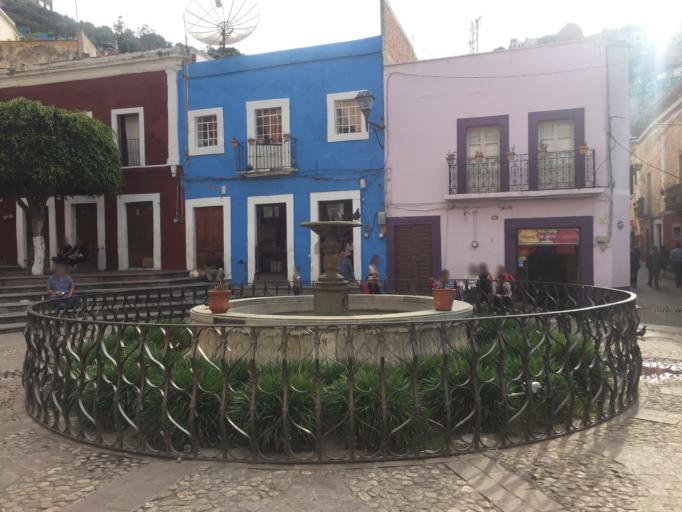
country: MX
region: Guanajuato
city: Guanajuato
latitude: 21.0167
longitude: -101.2562
